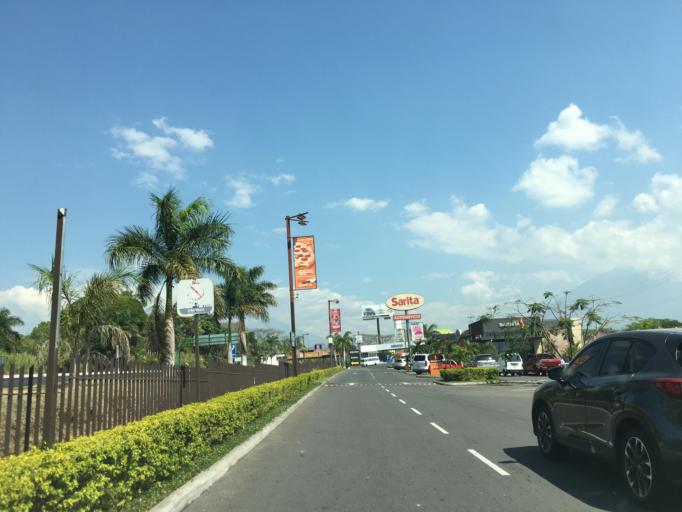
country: GT
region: Escuintla
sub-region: Municipio de Escuintla
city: Escuintla
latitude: 14.2949
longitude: -90.7993
